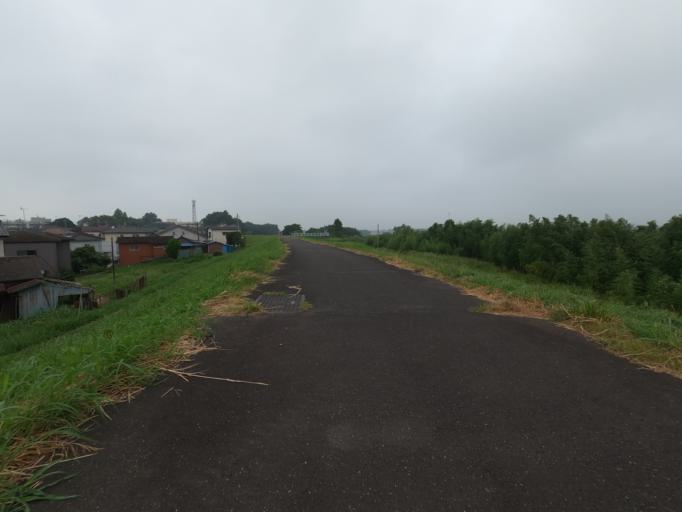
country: JP
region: Ibaraki
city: Mitsukaido
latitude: 36.0203
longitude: 139.9836
